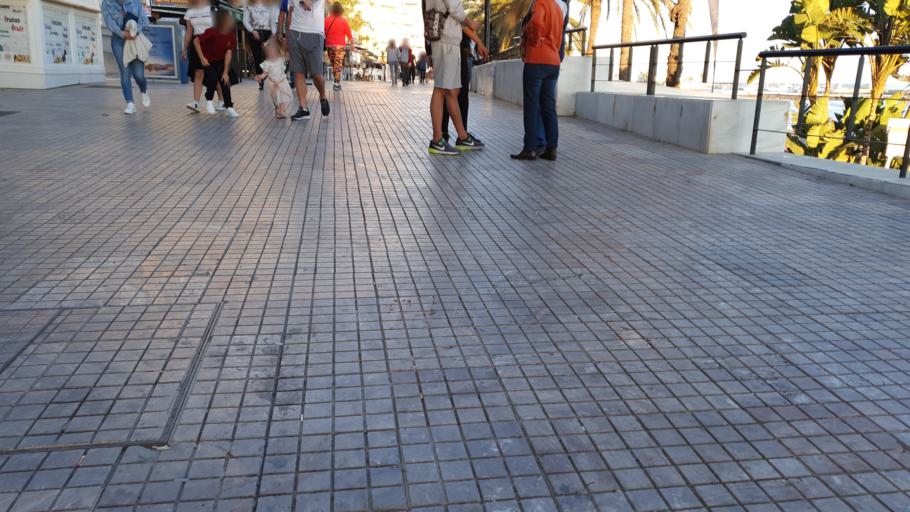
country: ES
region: Andalusia
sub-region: Provincia de Malaga
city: Marbella
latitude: 36.5069
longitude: -4.8966
